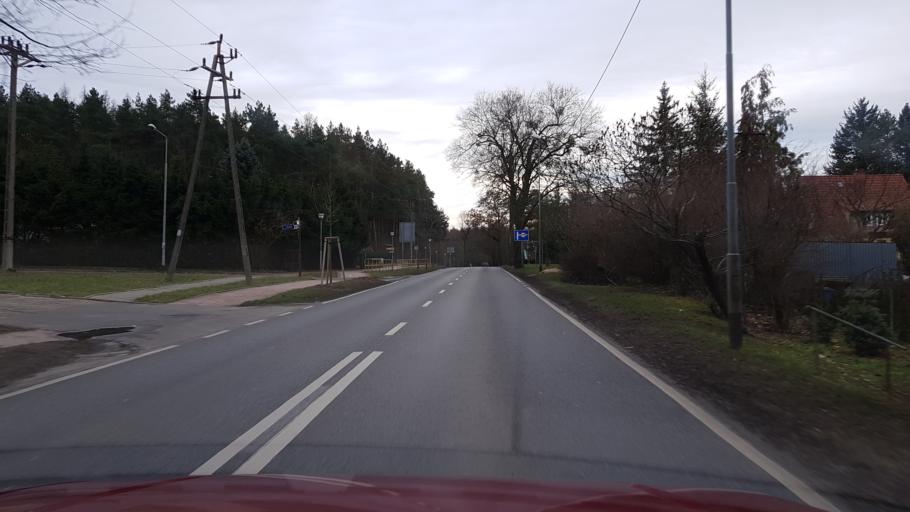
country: PL
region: West Pomeranian Voivodeship
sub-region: Powiat policki
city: Dobra
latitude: 53.4925
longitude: 14.4809
